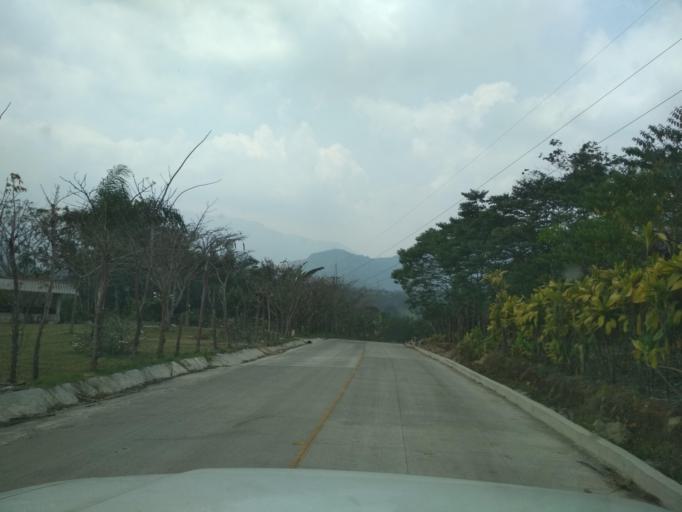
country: MX
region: Veracruz
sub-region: Cordoba
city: San Jose de Tapia
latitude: 18.8340
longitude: -96.9774
